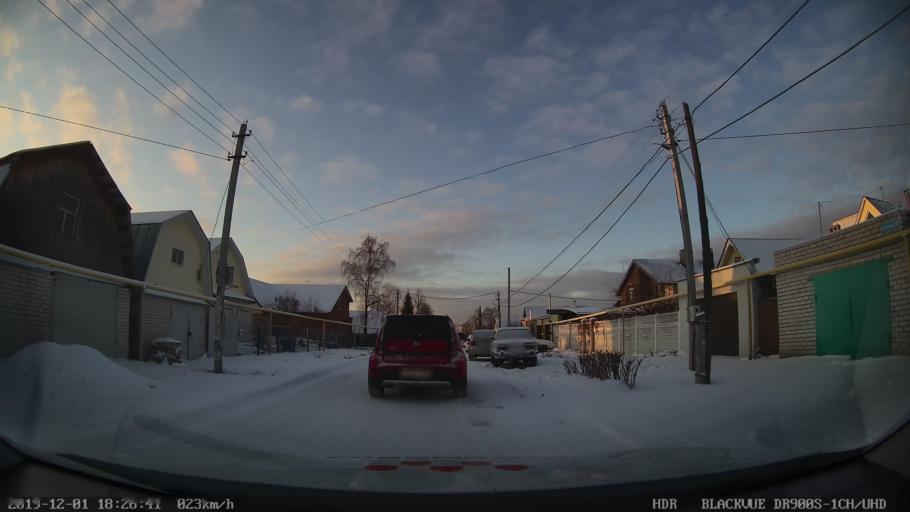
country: RU
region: Tatarstan
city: Vysokaya Gora
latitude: 55.8066
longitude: 49.2562
